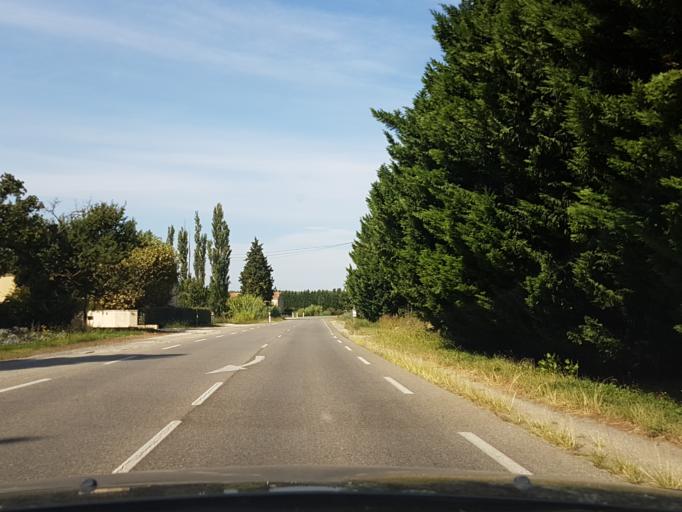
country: FR
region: Provence-Alpes-Cote d'Azur
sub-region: Departement des Bouches-du-Rhone
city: Noves
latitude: 43.8637
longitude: 4.9005
